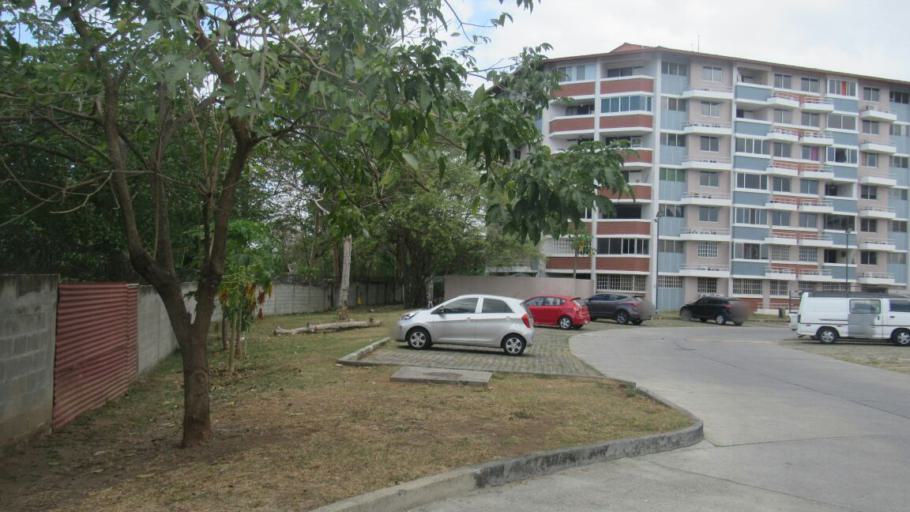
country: PA
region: Panama
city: San Miguelito
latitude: 9.0349
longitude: -79.4643
